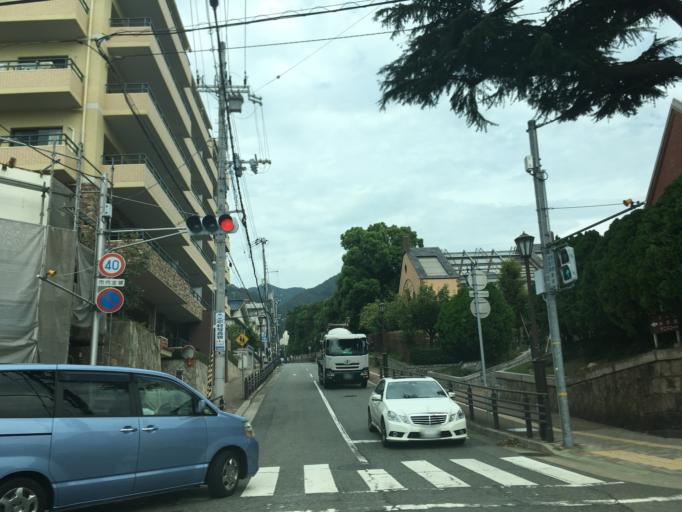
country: JP
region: Hyogo
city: Kobe
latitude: 34.7088
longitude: 135.2128
